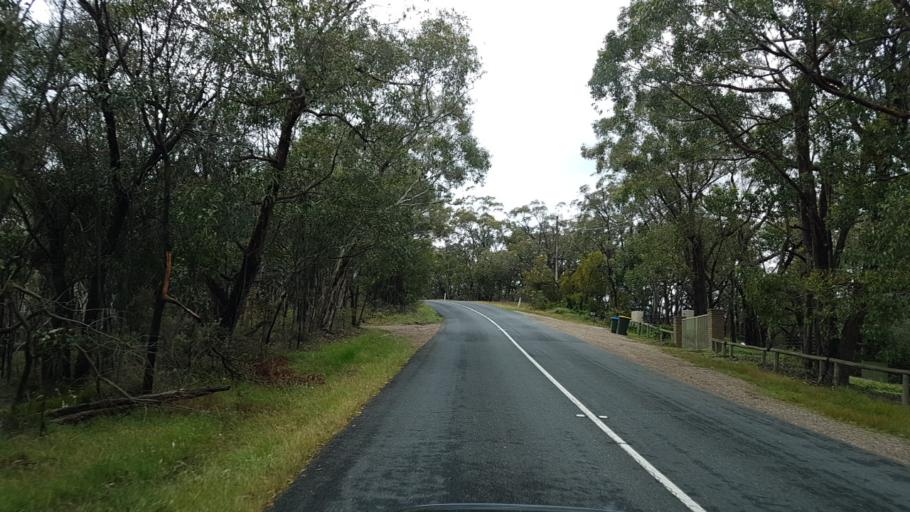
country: AU
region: South Australia
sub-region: Adelaide Hills
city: Adelaide Hills
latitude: -34.8981
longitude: 138.7563
